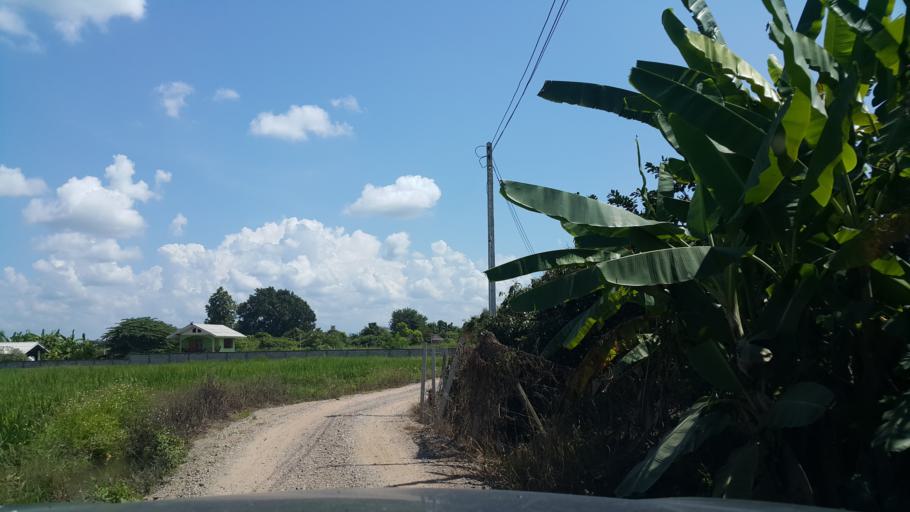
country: TH
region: Chiang Mai
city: Chom Thong
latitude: 18.4185
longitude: 98.6824
